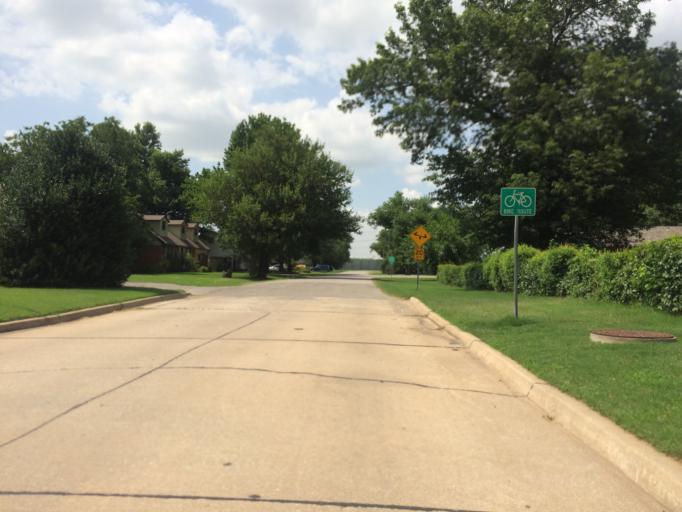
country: US
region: Oklahoma
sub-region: Cleveland County
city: Norman
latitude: 35.2146
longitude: -97.4834
